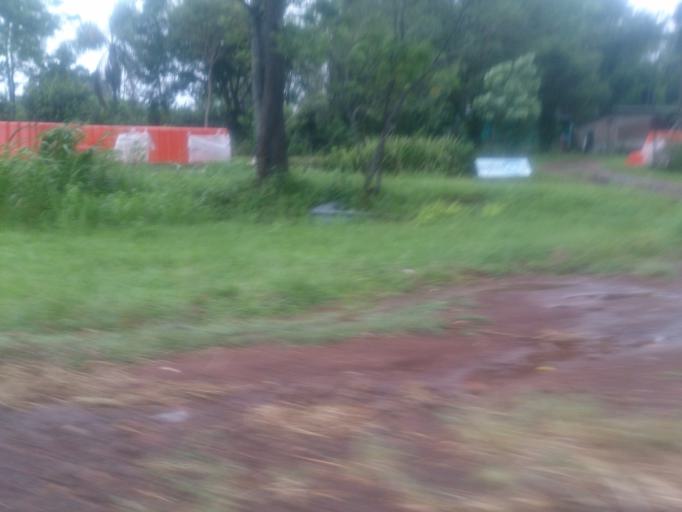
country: AR
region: Misiones
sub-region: Departamento de Obera
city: Obera
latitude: -27.4554
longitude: -55.0851
